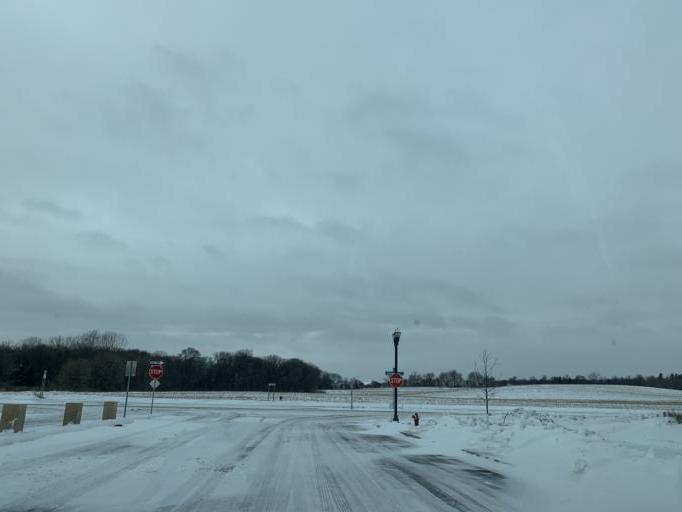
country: US
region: Minnesota
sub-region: Washington County
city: Cottage Grove
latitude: 44.8575
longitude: -92.9228
